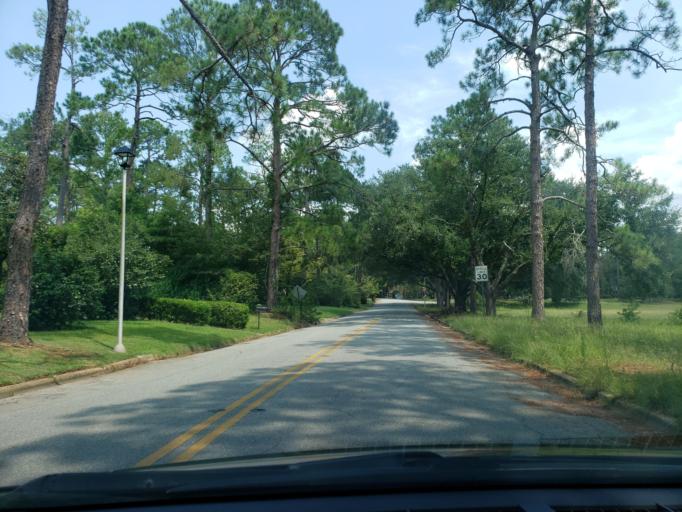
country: US
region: Georgia
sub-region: Dougherty County
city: Albany
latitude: 31.5954
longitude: -84.2031
